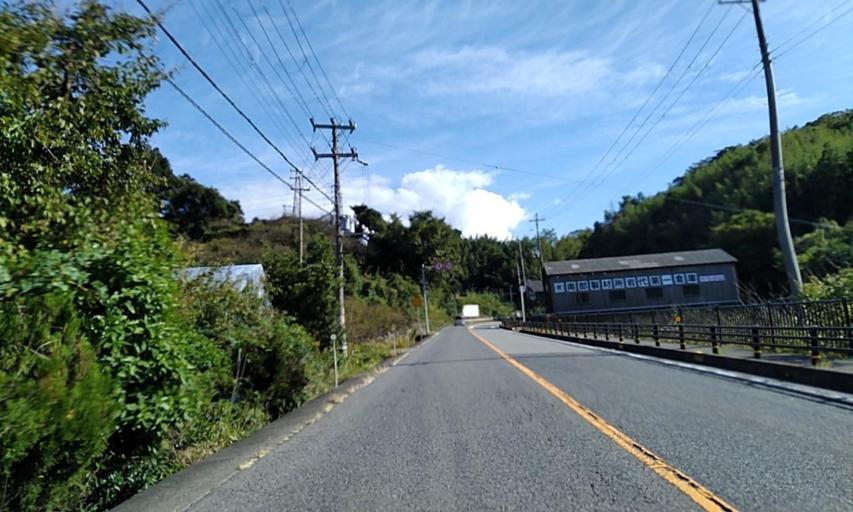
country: JP
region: Wakayama
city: Tanabe
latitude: 33.7816
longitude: 135.2889
